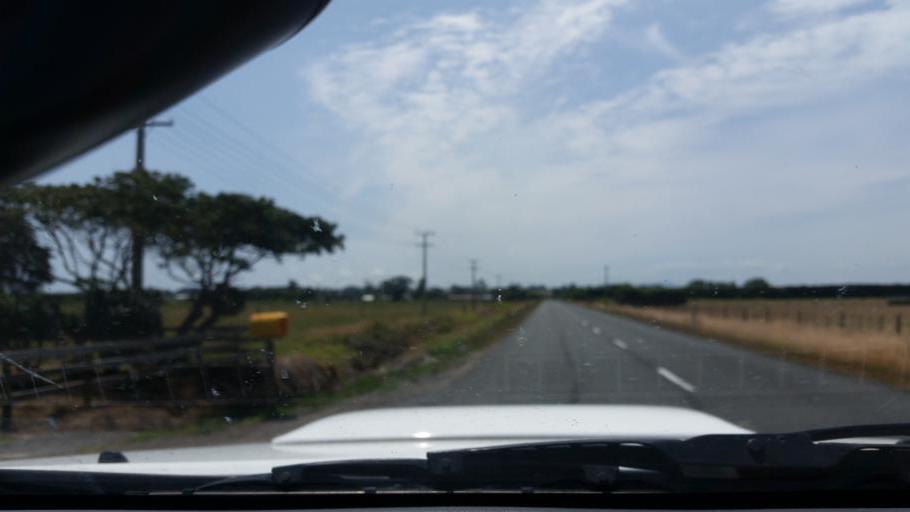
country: NZ
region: Northland
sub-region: Kaipara District
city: Dargaville
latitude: -36.0516
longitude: 173.9299
